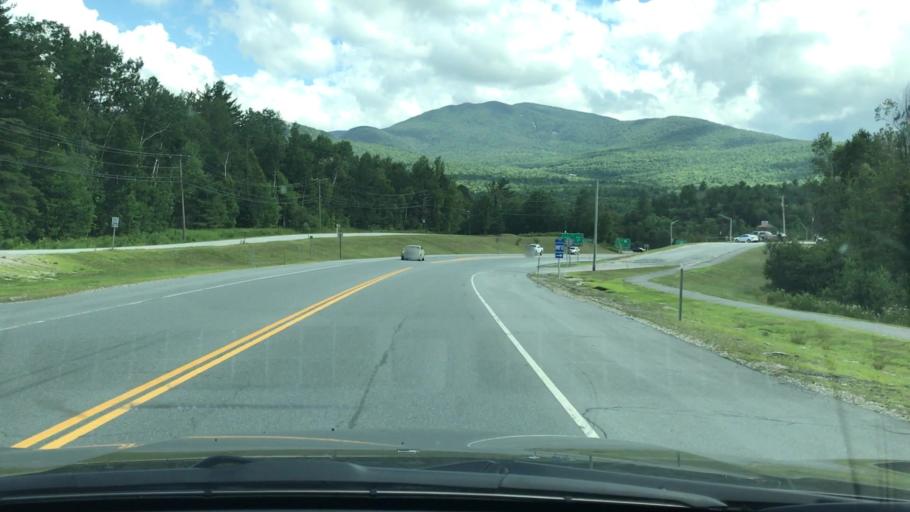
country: US
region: New Hampshire
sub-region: Grafton County
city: Deerfield
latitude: 44.2737
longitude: -71.5402
